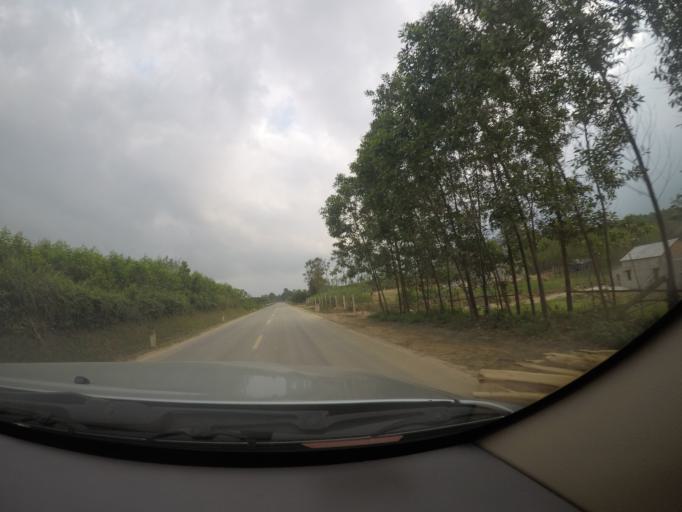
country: VN
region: Quang Tri
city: Ho Xa
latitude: 17.0590
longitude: 106.8624
